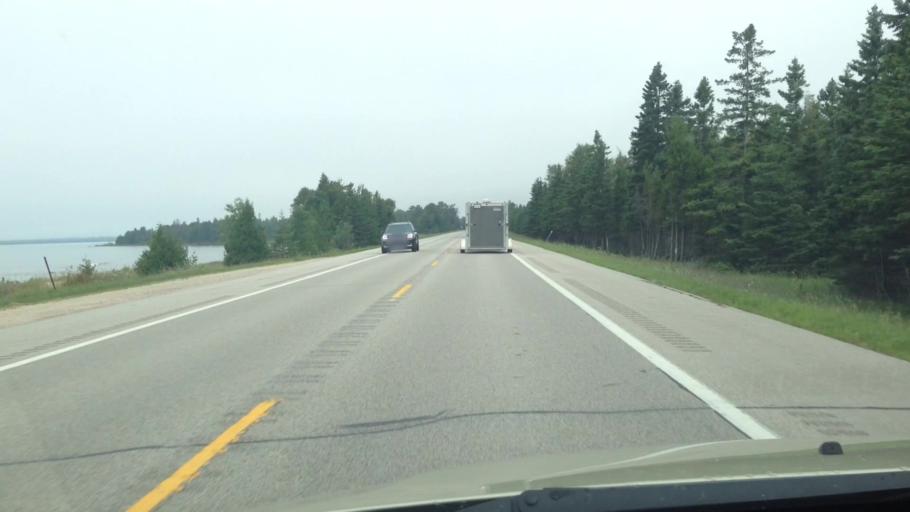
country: US
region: Michigan
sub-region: Luce County
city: Newberry
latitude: 46.0781
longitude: -85.2960
